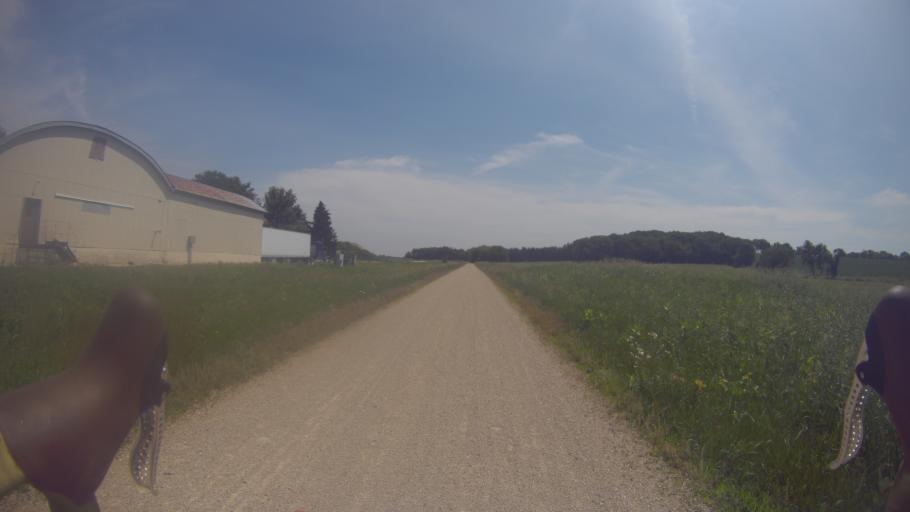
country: US
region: Wisconsin
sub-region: Jefferson County
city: Lake Mills
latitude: 43.0640
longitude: -88.9609
